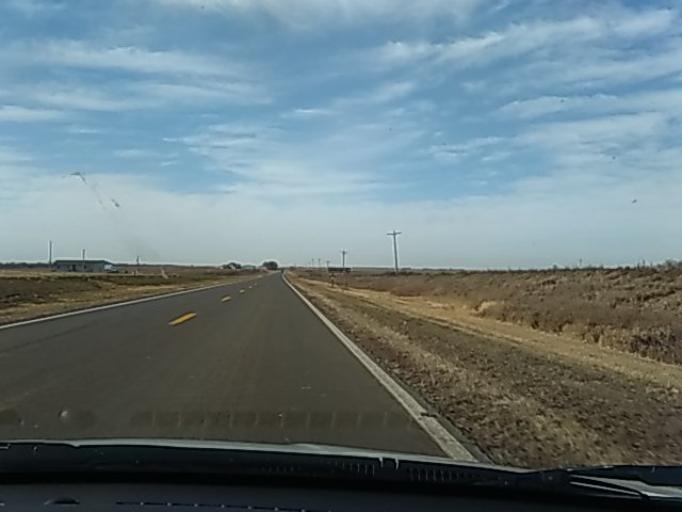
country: US
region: Nebraska
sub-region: Clay County
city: Clay Center
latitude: 40.4232
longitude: -97.9733
